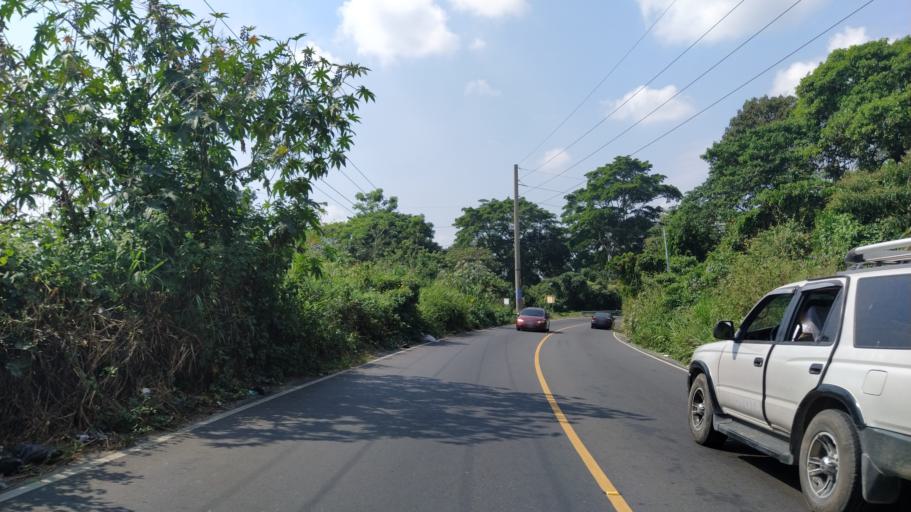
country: GT
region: Retalhuleu
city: San Felipe
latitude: 14.6199
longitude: -91.5868
